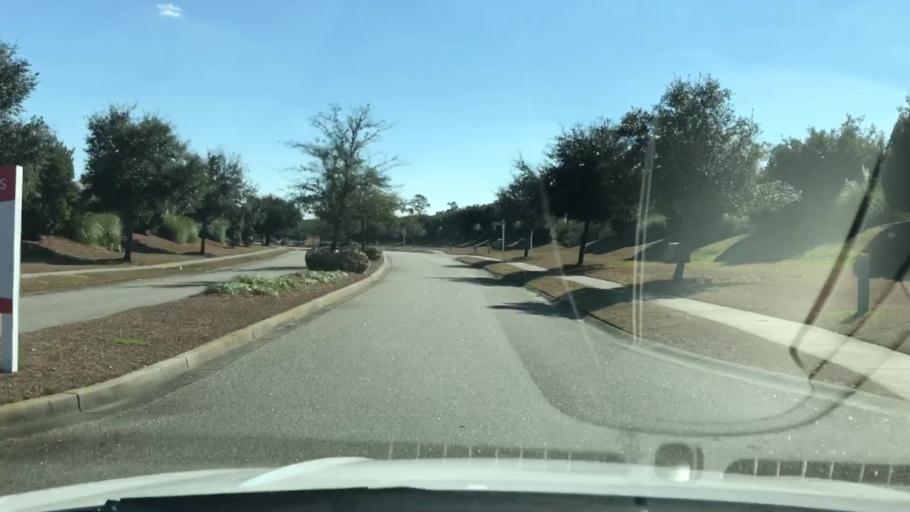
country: US
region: South Carolina
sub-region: Horry County
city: Socastee
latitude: 33.6447
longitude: -79.0369
